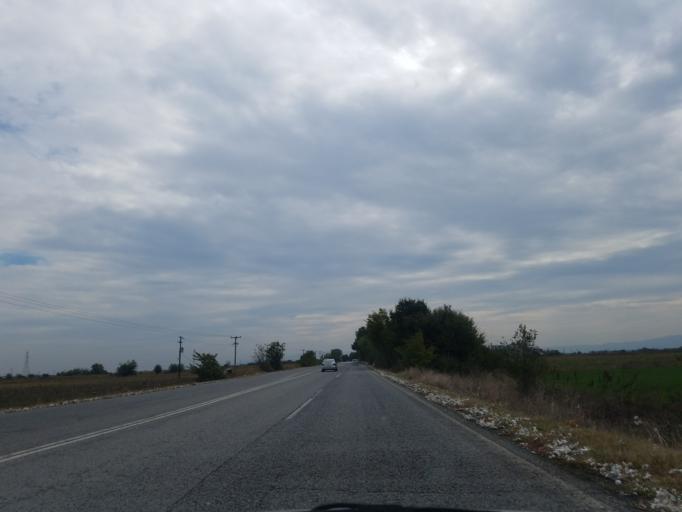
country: GR
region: Thessaly
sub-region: Nomos Kardhitsas
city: Karpochori
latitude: 39.3592
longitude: 22.0435
